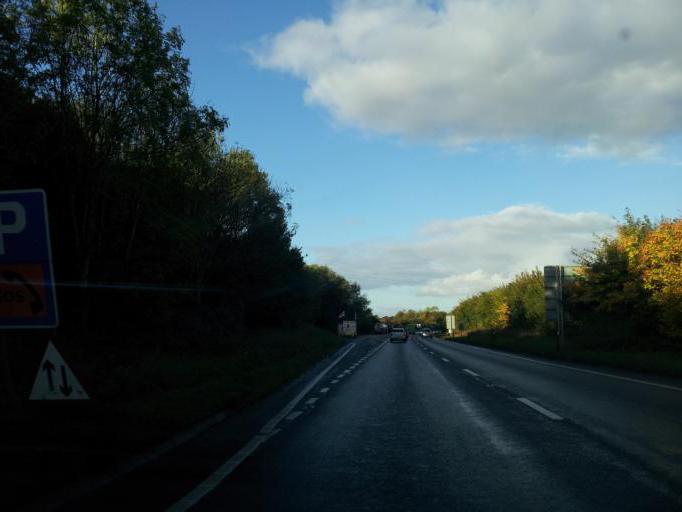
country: GB
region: England
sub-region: Norfolk
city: Hethersett
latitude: 52.6551
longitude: 1.1461
